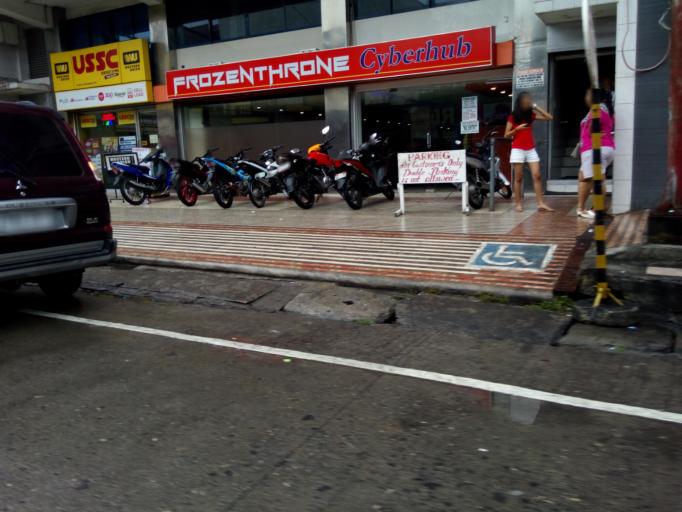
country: PH
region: Central Visayas
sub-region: Province of Negros Oriental
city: Dumaguete
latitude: 9.3099
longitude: 123.3075
